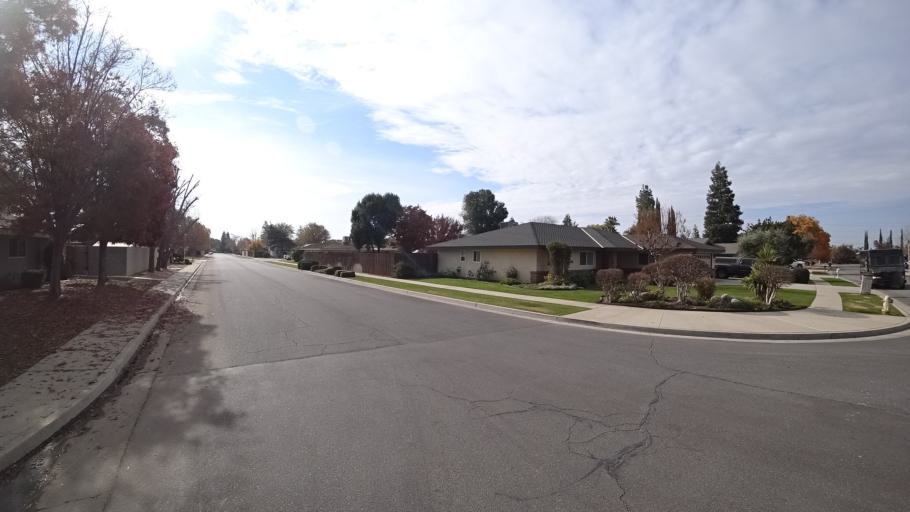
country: US
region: California
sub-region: Kern County
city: Greenacres
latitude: 35.4113
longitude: -119.0900
